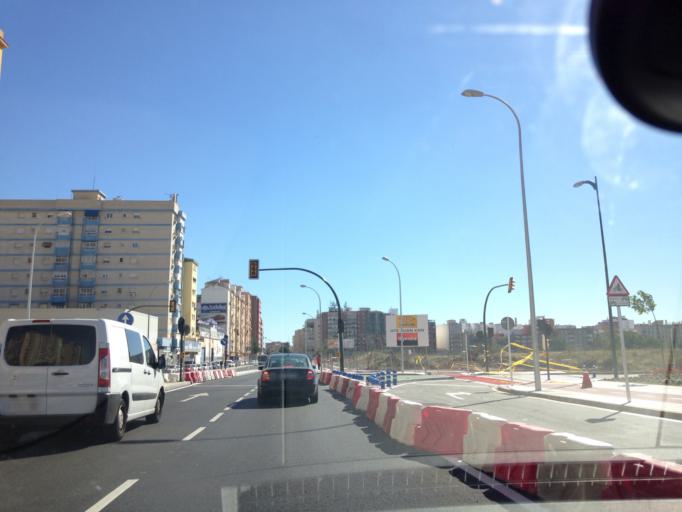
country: ES
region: Andalusia
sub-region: Provincia de Malaga
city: Malaga
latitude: 36.7073
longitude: -4.4433
